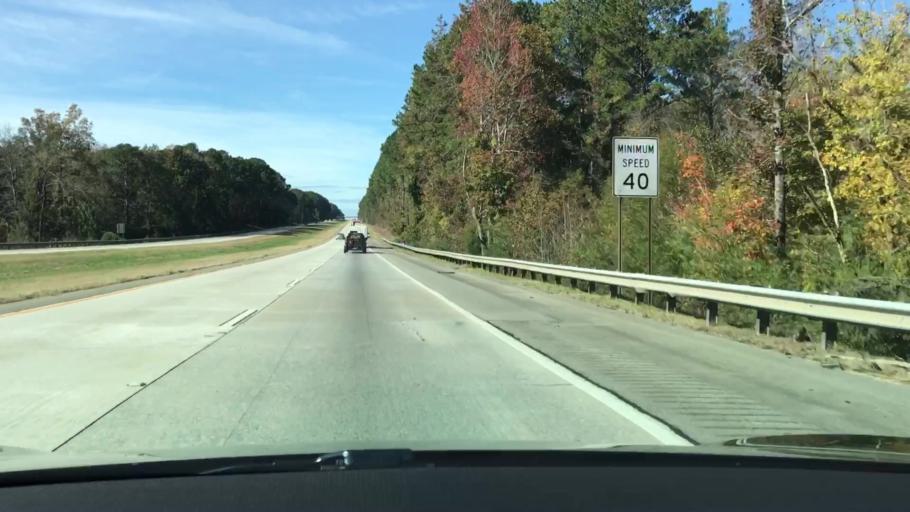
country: US
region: Georgia
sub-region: Greene County
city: Greensboro
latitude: 33.5491
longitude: -83.1454
